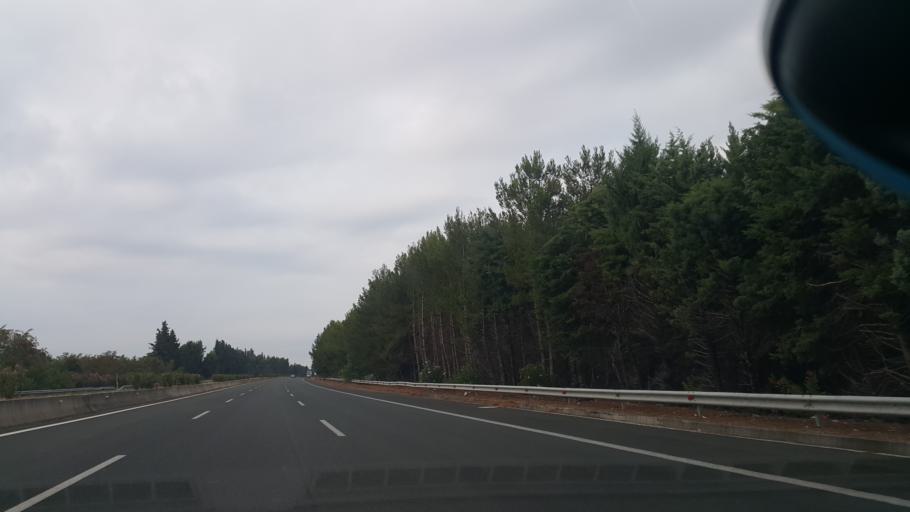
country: GR
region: Central Macedonia
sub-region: Nomos Pierias
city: Kitros
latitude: 40.3704
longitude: 22.6057
